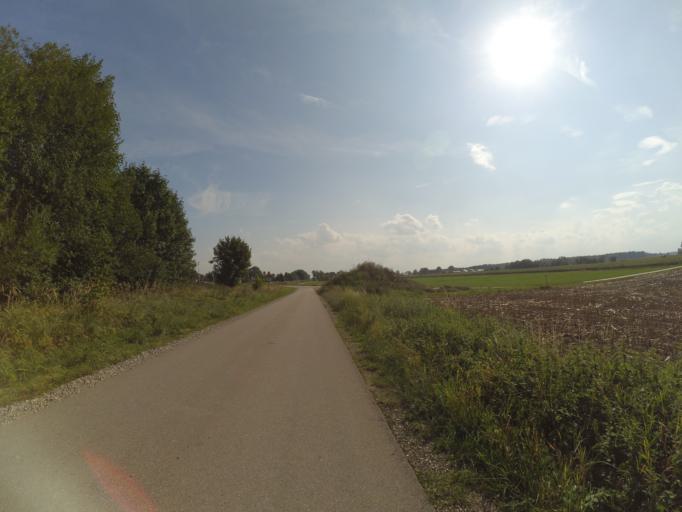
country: DE
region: Bavaria
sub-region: Swabia
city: Lamerdingen
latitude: 48.0661
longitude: 10.7281
